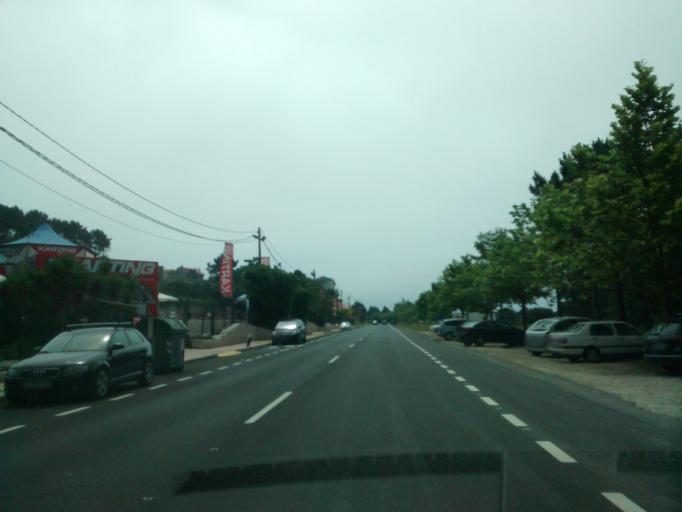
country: ES
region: Galicia
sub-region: Provincia de Pontevedra
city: Sanxenxo
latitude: 42.4154
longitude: -8.8672
